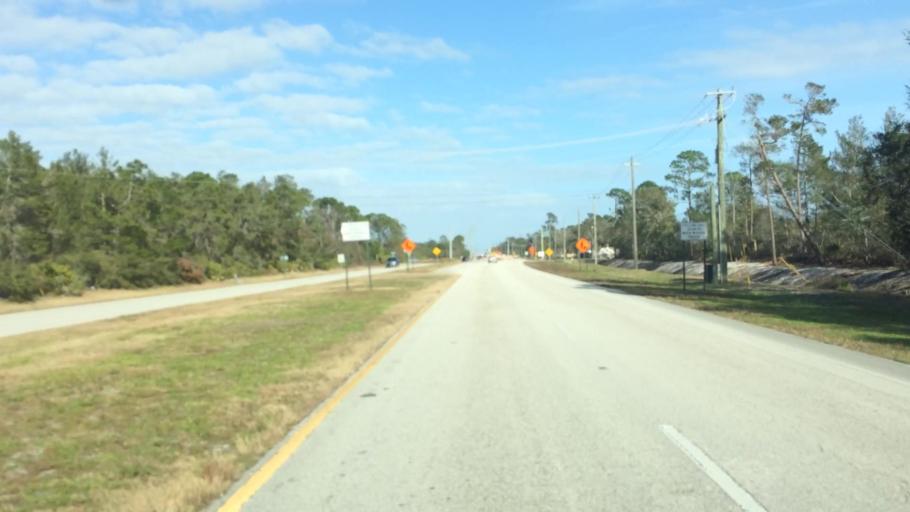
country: US
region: Florida
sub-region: Volusia County
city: Holly Hill
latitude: 29.2313
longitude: -81.0762
